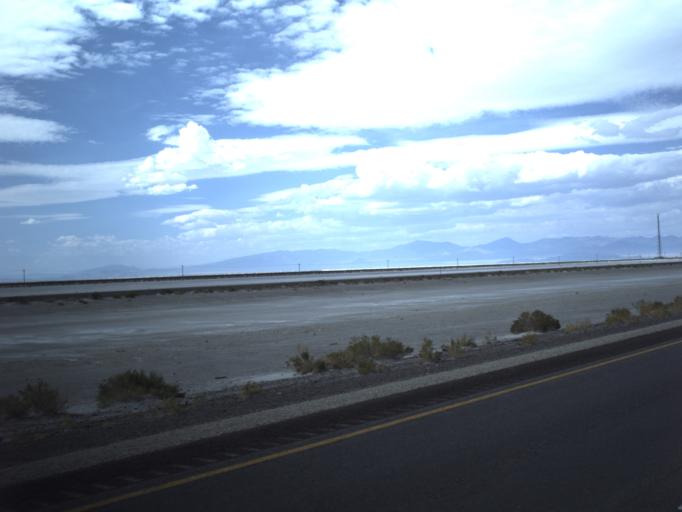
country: US
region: Utah
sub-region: Tooele County
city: Wendover
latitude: 40.7377
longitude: -113.7698
